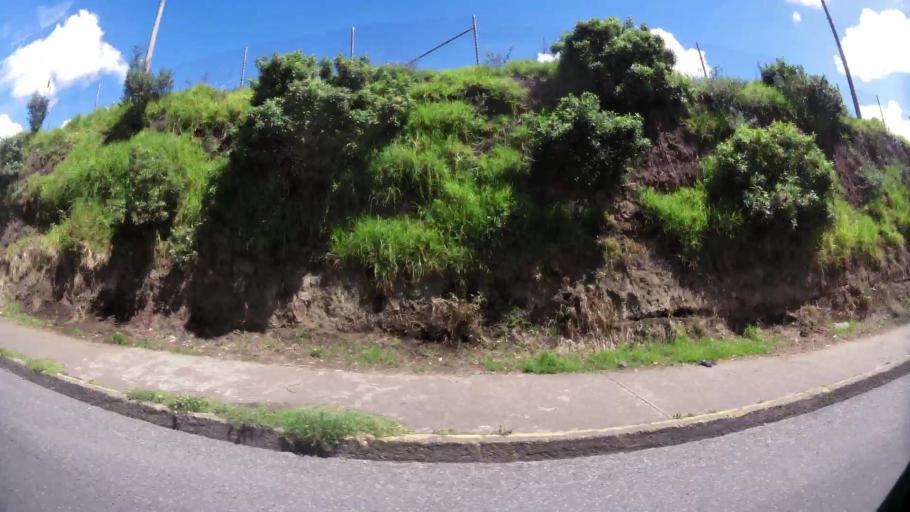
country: EC
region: Pichincha
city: Quito
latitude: -0.3183
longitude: -78.5635
